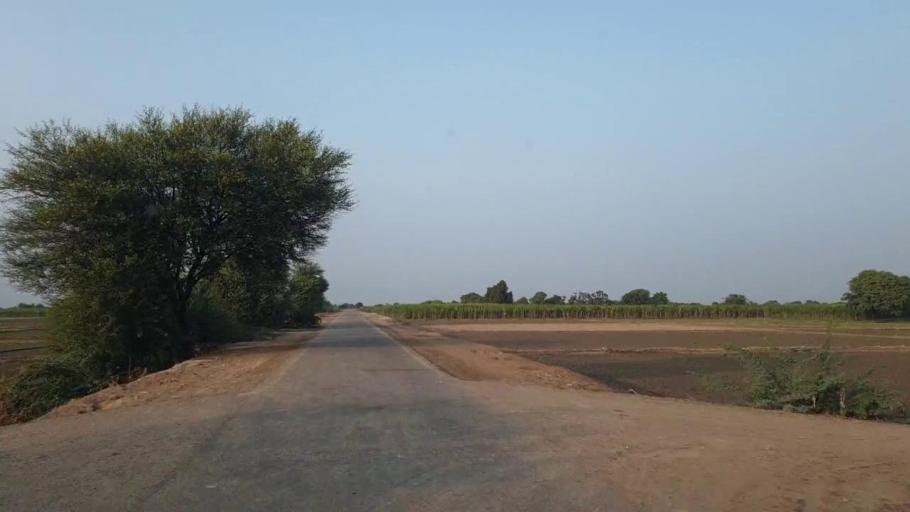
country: PK
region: Sindh
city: Tando Ghulam Ali
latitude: 25.0901
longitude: 68.9586
